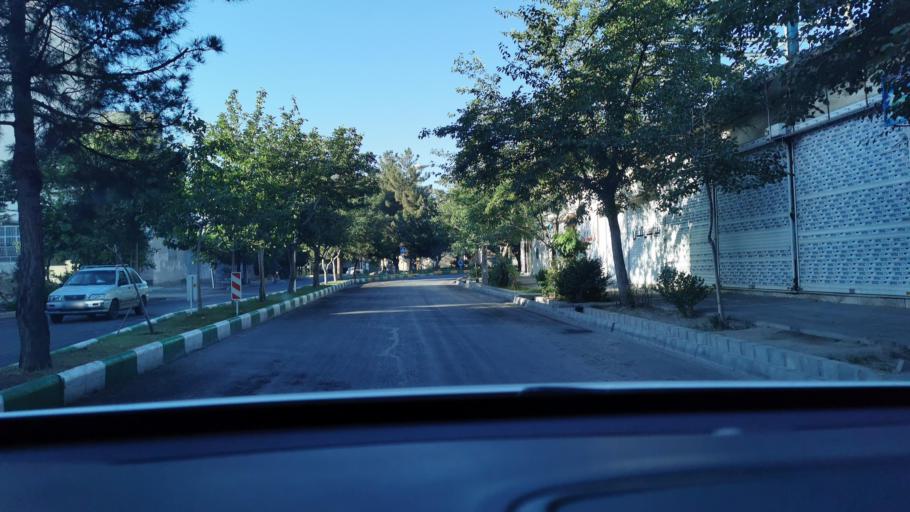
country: IR
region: Razavi Khorasan
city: Mashhad
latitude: 36.3609
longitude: 59.4904
